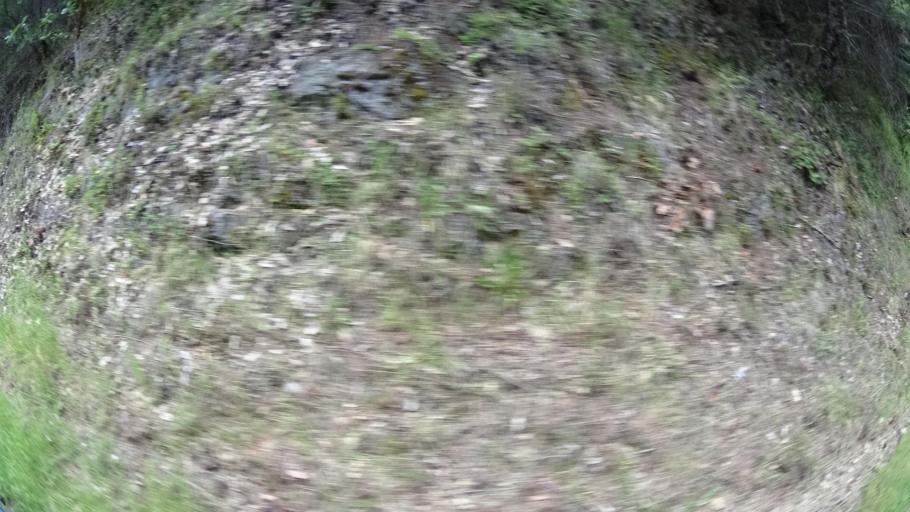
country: US
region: California
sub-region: Humboldt County
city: Blue Lake
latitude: 40.7625
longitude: -123.9247
